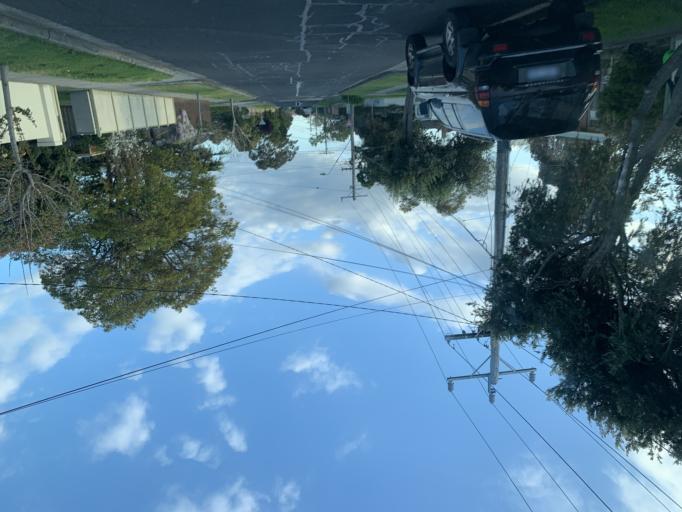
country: AU
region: Victoria
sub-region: Kingston
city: Parkdale
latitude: -37.9831
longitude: 145.0845
